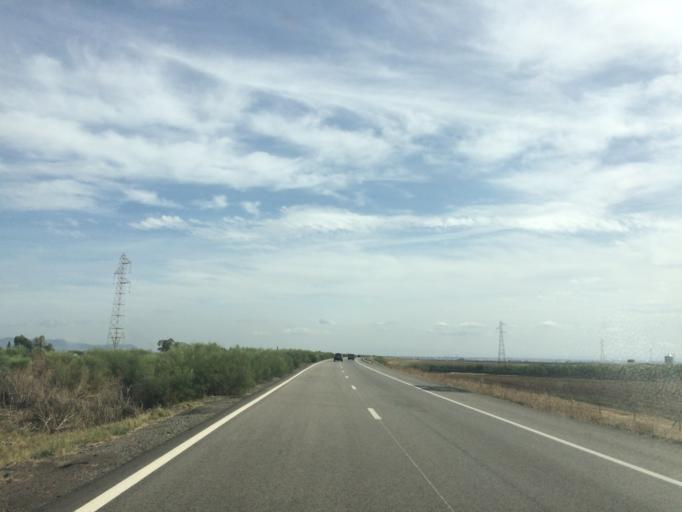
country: MA
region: Meknes-Tafilalet
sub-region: Meknes
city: Meknes
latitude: 33.8948
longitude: -5.6863
